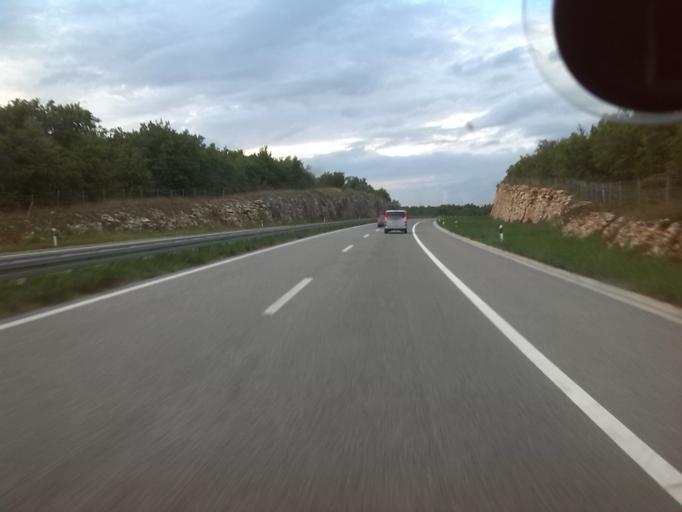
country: HR
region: Istarska
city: Buje
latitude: 45.3857
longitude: 13.6166
